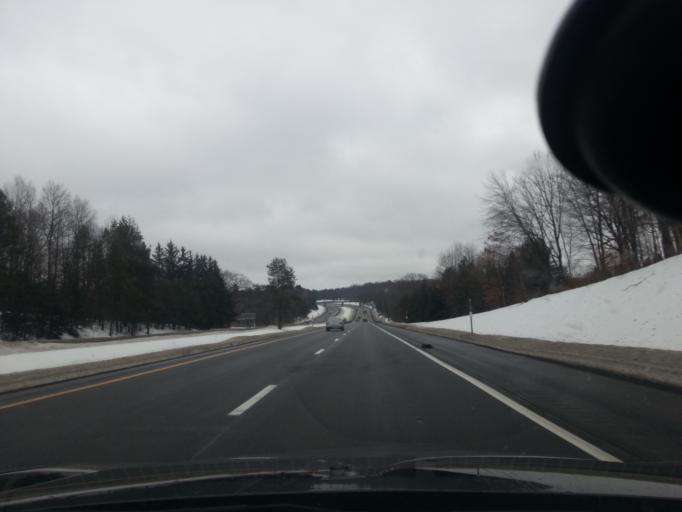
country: US
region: New York
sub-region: Oswego County
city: Central Square
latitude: 43.3801
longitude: -76.1211
